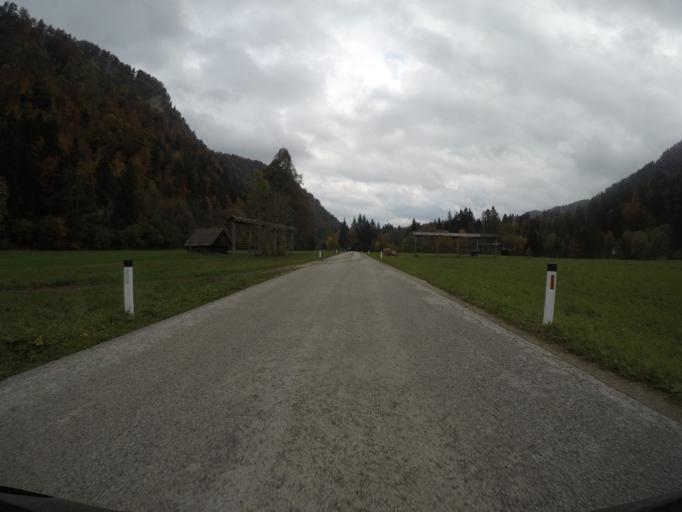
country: SI
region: Gorje
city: Zgornje Gorje
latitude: 46.3834
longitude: 14.0430
